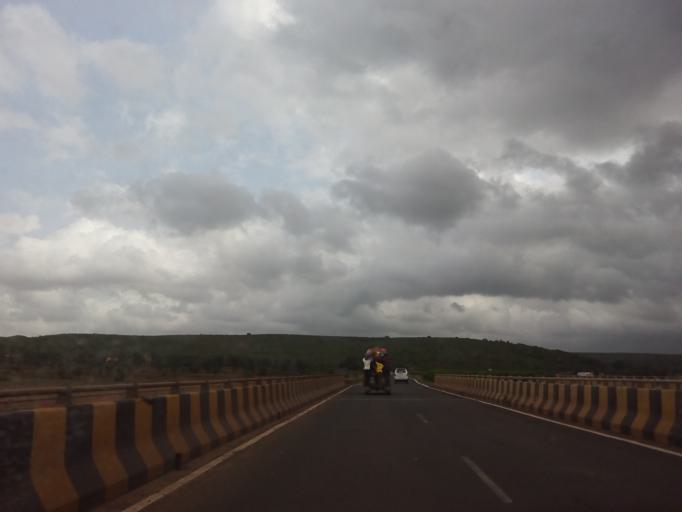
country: IN
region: Karnataka
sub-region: Belgaum
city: Hukeri
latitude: 16.0707
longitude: 74.5184
